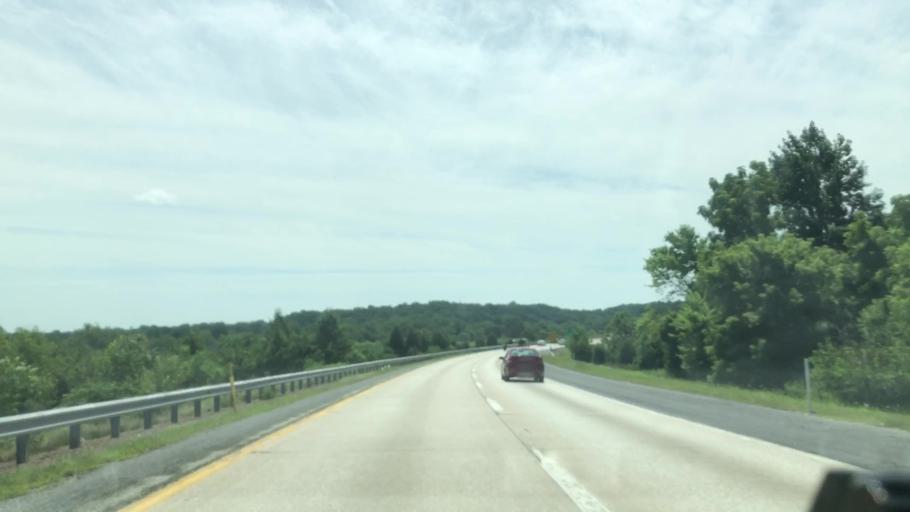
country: US
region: Pennsylvania
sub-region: Montgomery County
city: Audubon
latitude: 40.1370
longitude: -75.4482
